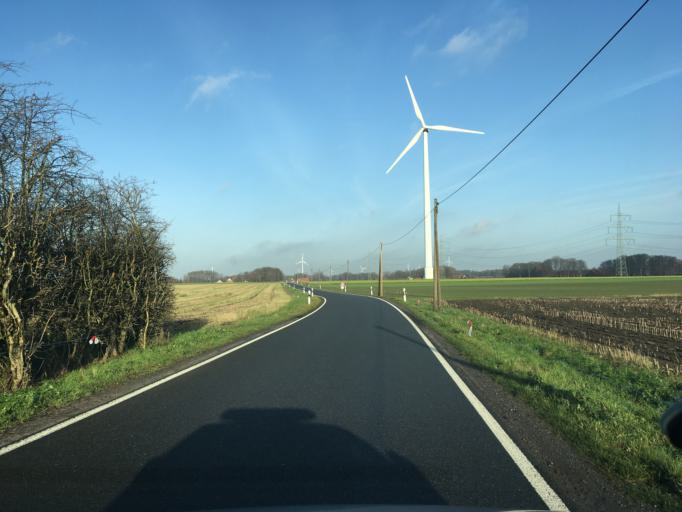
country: DE
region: North Rhine-Westphalia
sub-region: Regierungsbezirk Munster
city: Velen
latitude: 51.9225
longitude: 6.9635
